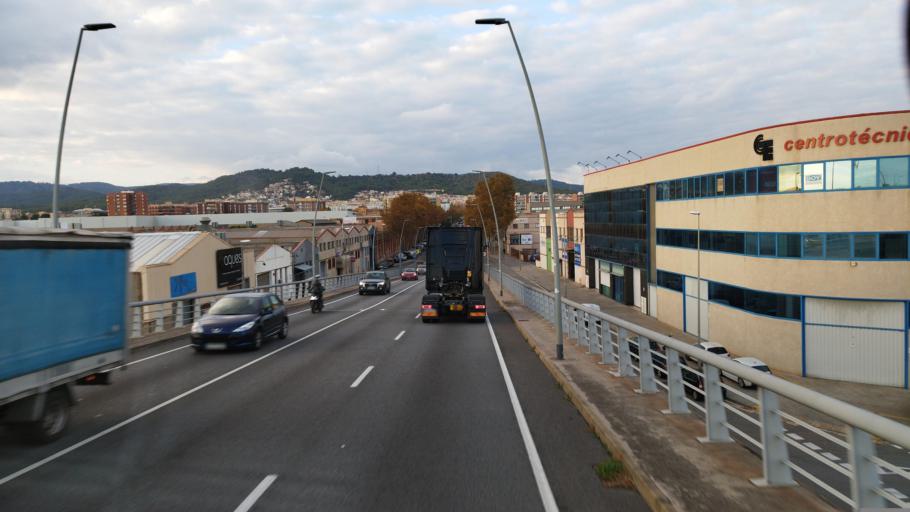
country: ES
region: Catalonia
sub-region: Provincia de Barcelona
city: Viladecans
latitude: 41.3076
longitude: 2.0206
